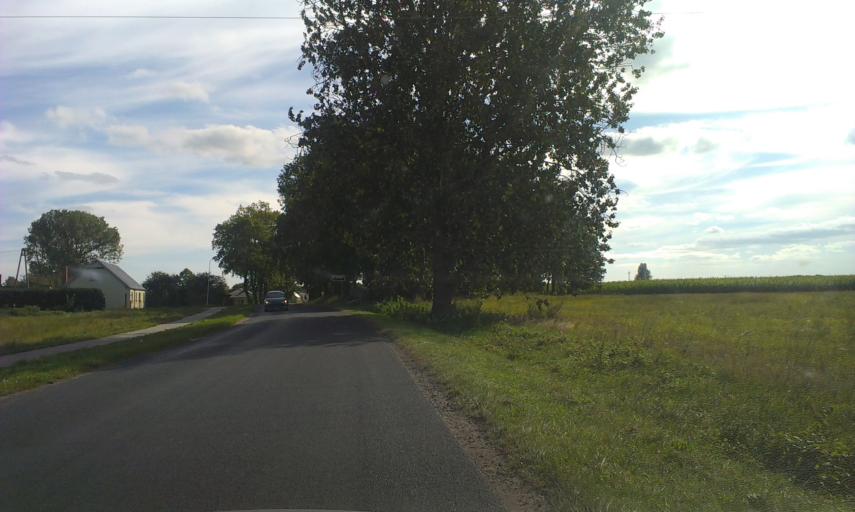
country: PL
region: Greater Poland Voivodeship
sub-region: Powiat zlotowski
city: Zlotow
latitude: 53.3432
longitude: 17.0764
